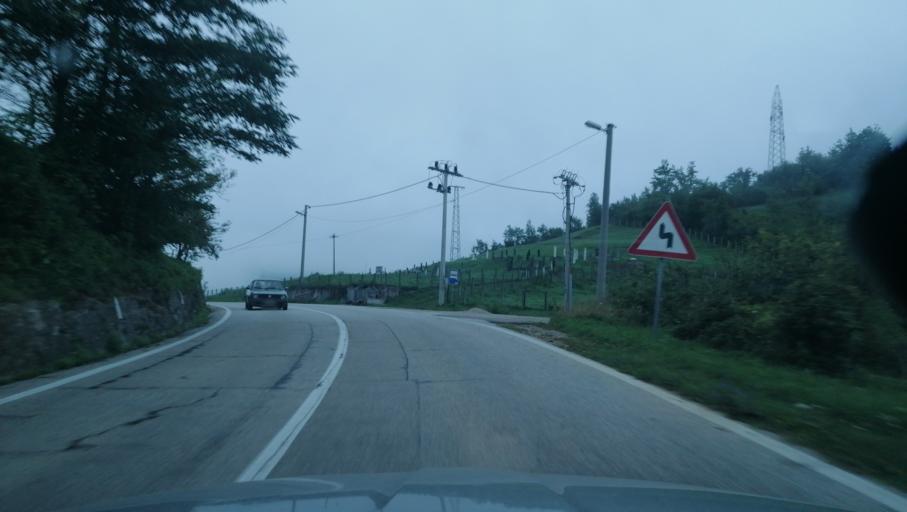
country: BA
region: Federation of Bosnia and Herzegovina
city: Jablanica
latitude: 43.7075
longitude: 17.7175
